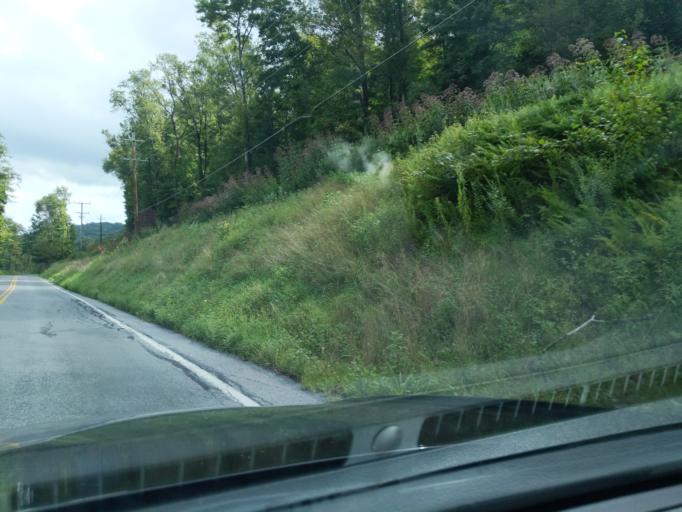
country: US
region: Pennsylvania
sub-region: Blair County
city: Claysburg
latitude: 40.3676
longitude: -78.5077
